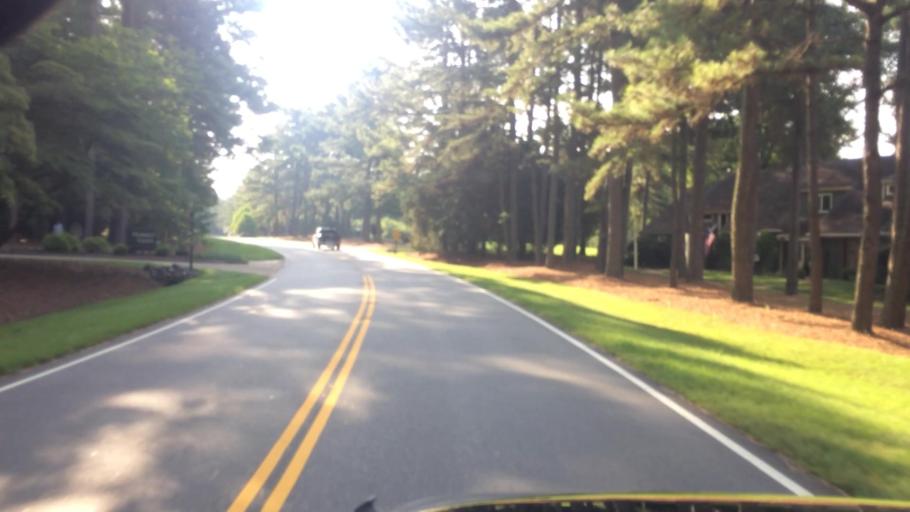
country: US
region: Virginia
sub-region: City of Williamsburg
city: Williamsburg
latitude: 37.2327
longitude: -76.6598
